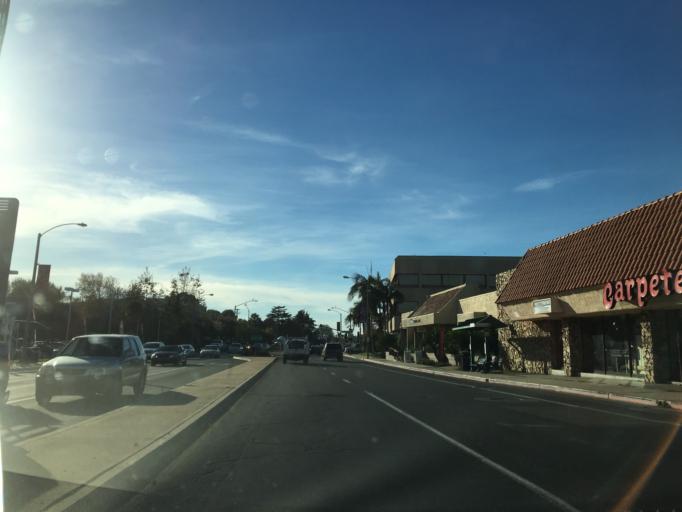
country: US
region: California
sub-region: Santa Barbara County
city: Goleta
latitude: 34.4358
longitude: -119.8206
